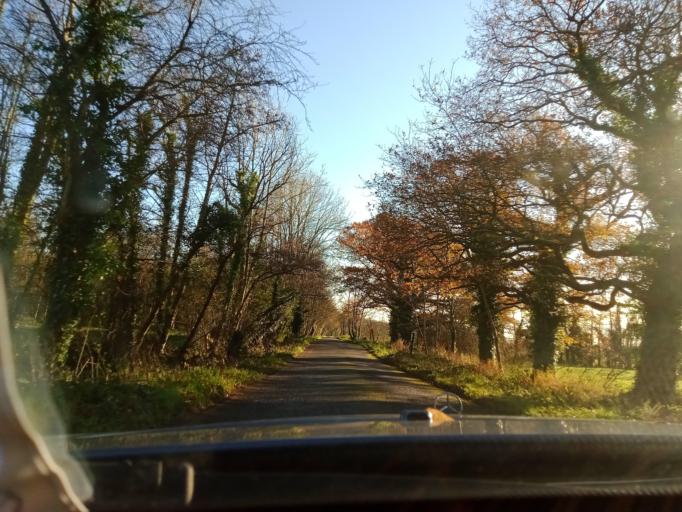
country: IE
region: Leinster
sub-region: Kilkenny
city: Piltown
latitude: 52.3505
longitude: -7.2851
